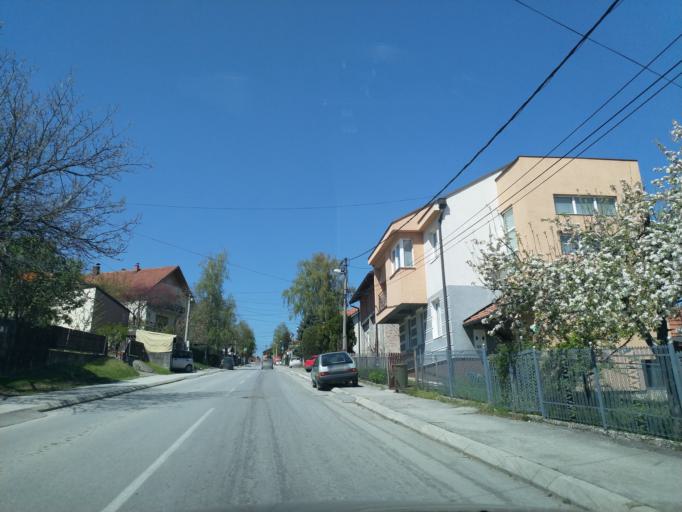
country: RS
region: Central Serbia
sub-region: Kolubarski Okrug
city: Valjevo
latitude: 44.2739
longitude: 19.8772
